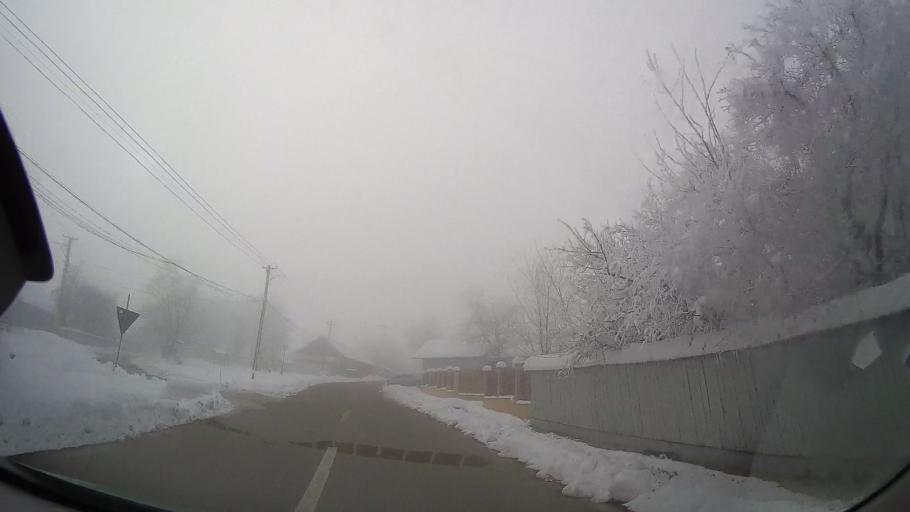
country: RO
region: Iasi
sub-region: Comuna Valea Seaca
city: Topile
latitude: 47.2662
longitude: 26.6703
